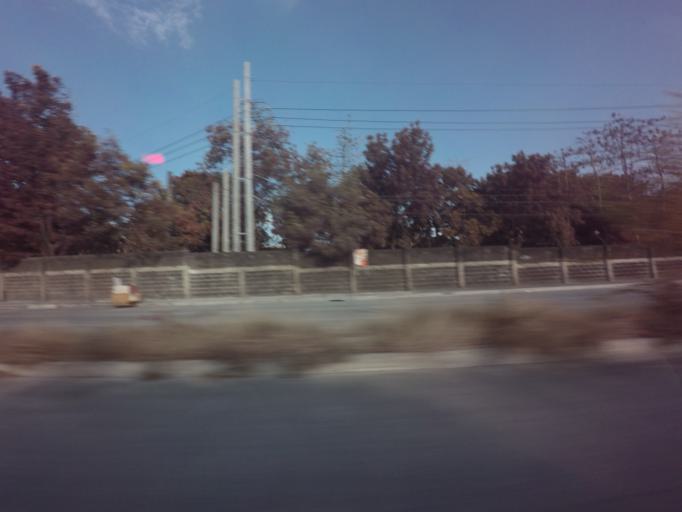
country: PH
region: Metro Manila
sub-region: Makati City
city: Makati City
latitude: 14.5043
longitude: 121.0214
